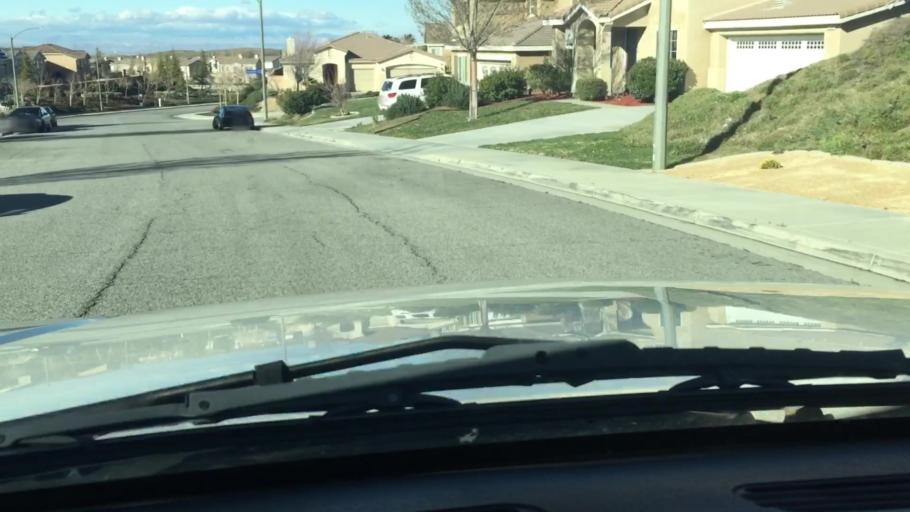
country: US
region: California
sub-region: Los Angeles County
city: Desert View Highlands
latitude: 34.5623
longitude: -118.1723
